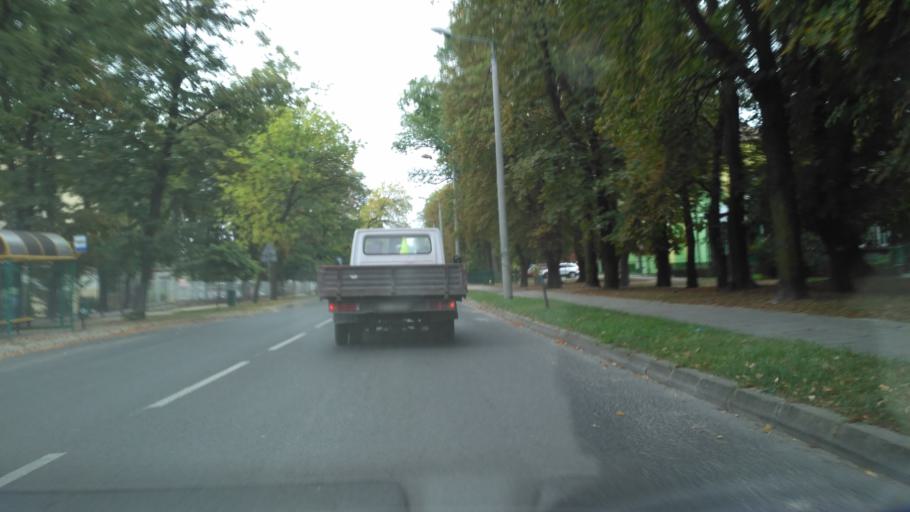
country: PL
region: Lublin Voivodeship
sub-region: Chelm
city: Chelm
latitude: 51.1415
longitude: 23.4507
